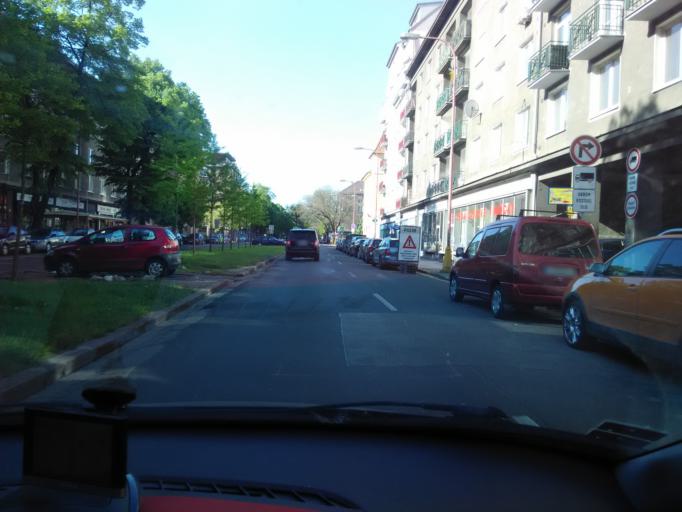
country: SK
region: Bratislavsky
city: Bratislava
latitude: 48.1507
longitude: 17.1350
